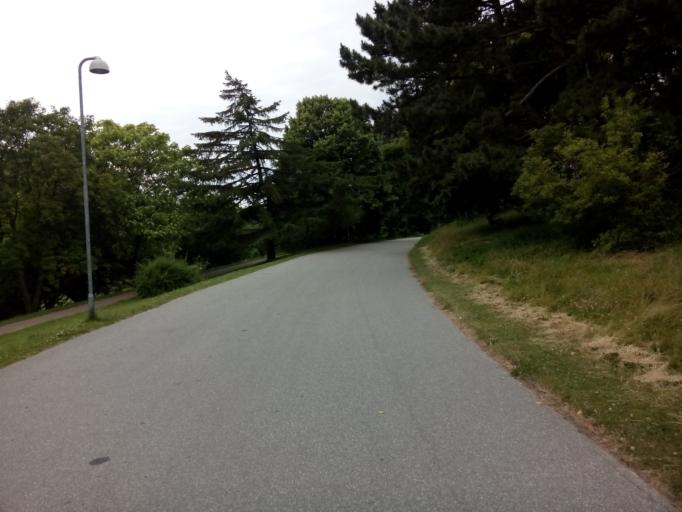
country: DK
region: Central Jutland
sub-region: Arhus Kommune
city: Arhus
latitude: 56.1618
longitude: 10.1914
